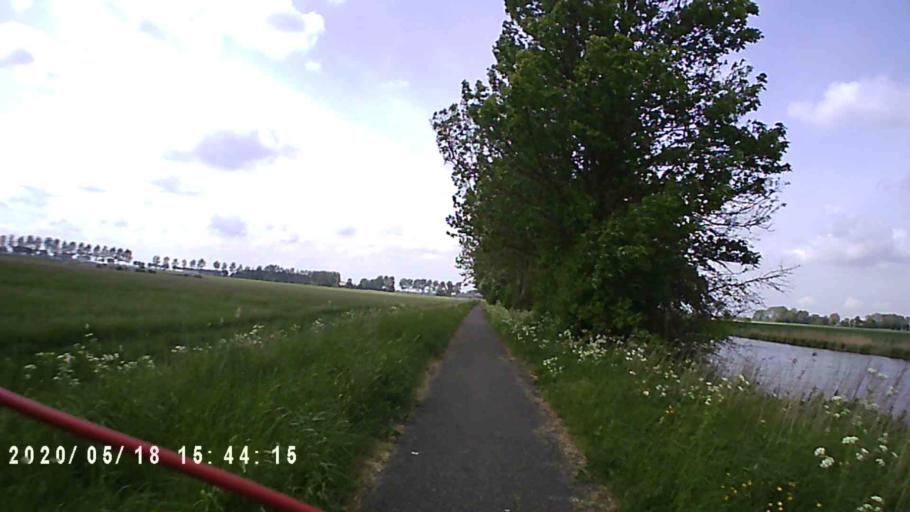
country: NL
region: Groningen
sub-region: Gemeente Winsum
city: Winsum
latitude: 53.3111
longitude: 6.4733
